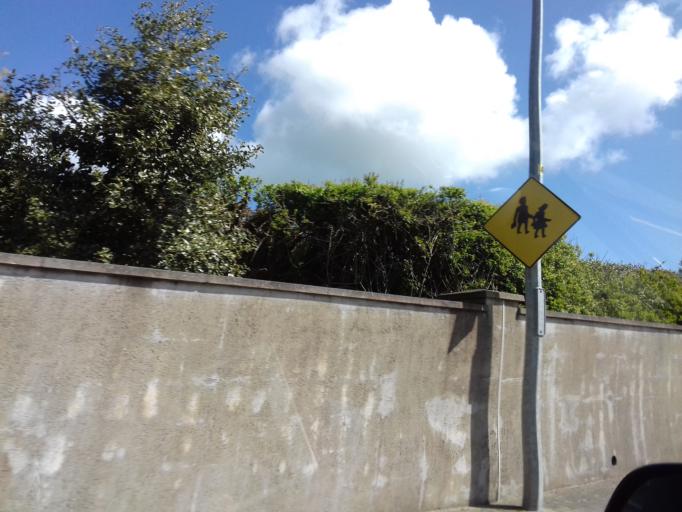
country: IE
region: Leinster
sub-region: Loch Garman
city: Castlebridge
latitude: 52.3933
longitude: -6.3931
